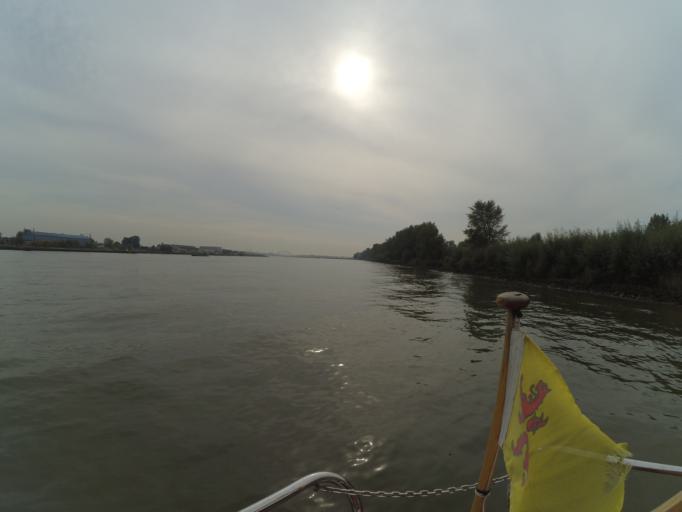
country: NL
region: South Holland
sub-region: Gemeente Ridderkerk
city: Ridderkerk
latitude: 51.8752
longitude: 4.6290
